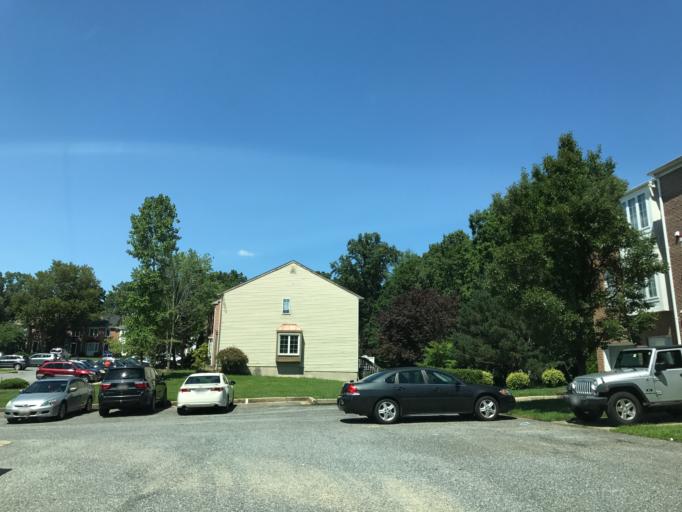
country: US
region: Maryland
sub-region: Baltimore County
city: Perry Hall
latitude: 39.3820
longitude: -76.4671
